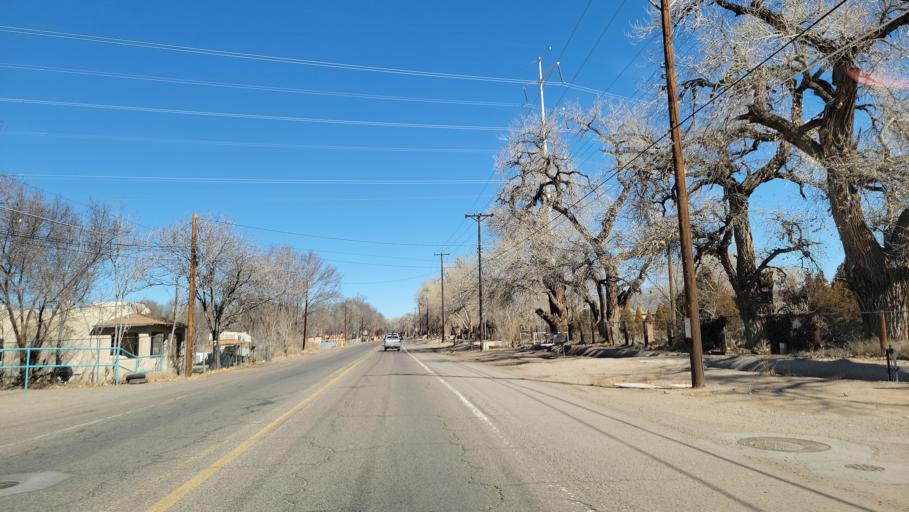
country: US
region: New Mexico
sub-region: Bernalillo County
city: South Valley
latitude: 35.0040
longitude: -106.6902
